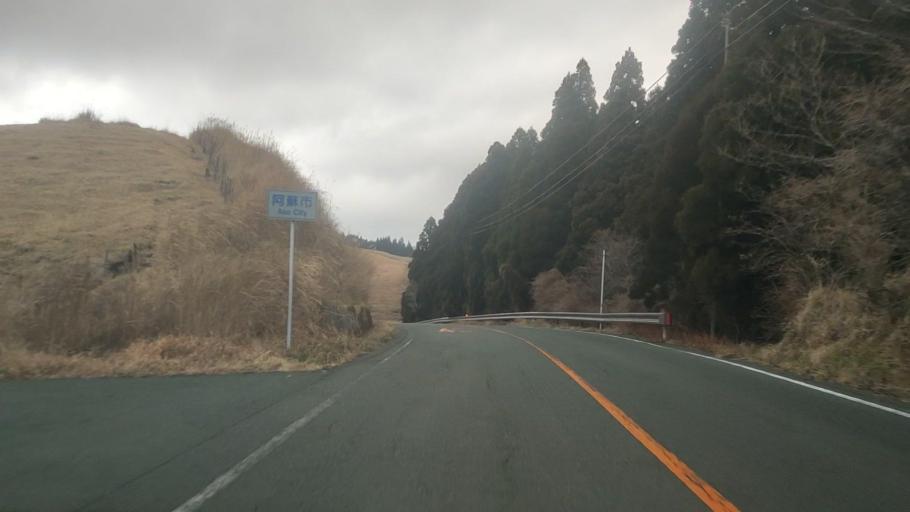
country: JP
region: Kumamoto
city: Aso
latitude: 32.8841
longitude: 131.1708
